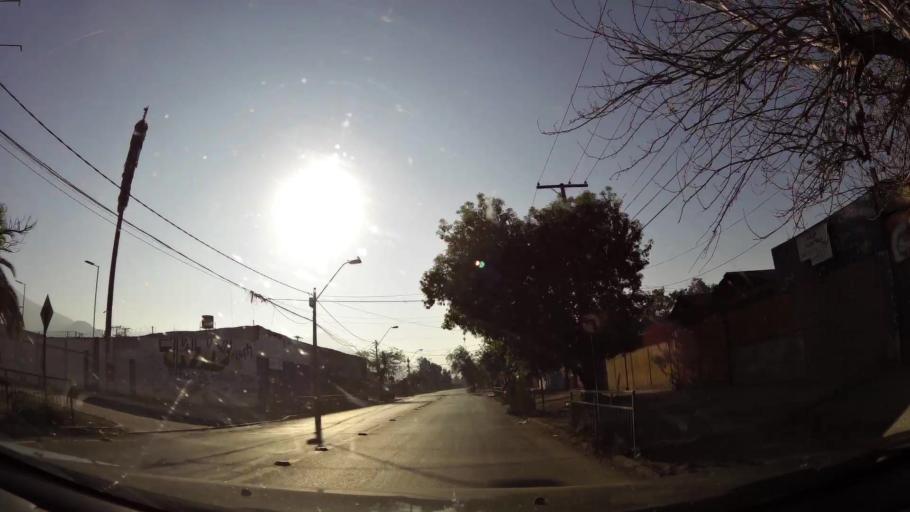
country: CL
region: Santiago Metropolitan
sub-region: Provincia de Santiago
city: Santiago
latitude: -33.3799
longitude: -70.6654
